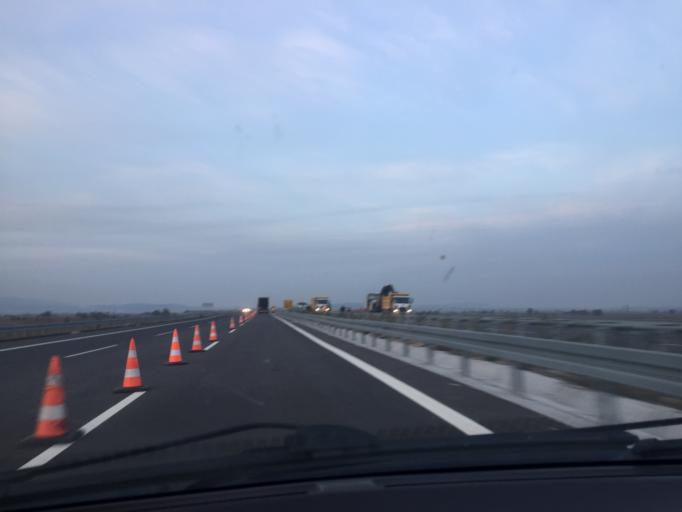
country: TR
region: Manisa
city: Halitpasa
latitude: 38.7230
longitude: 27.6524
